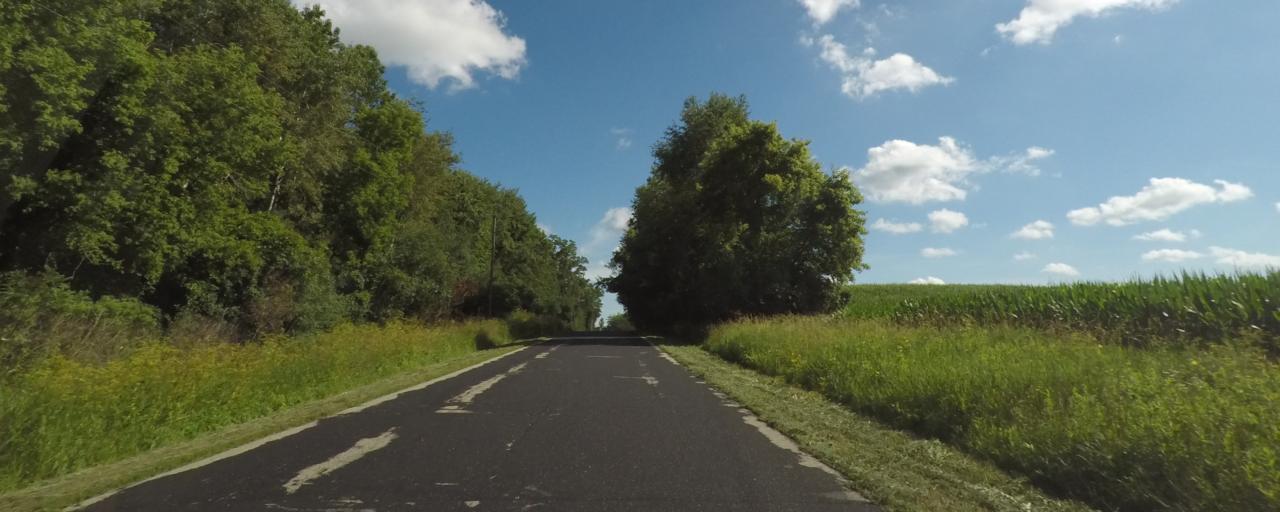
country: US
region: Wisconsin
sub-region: Rock County
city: Edgerton
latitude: 42.8722
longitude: -89.1321
